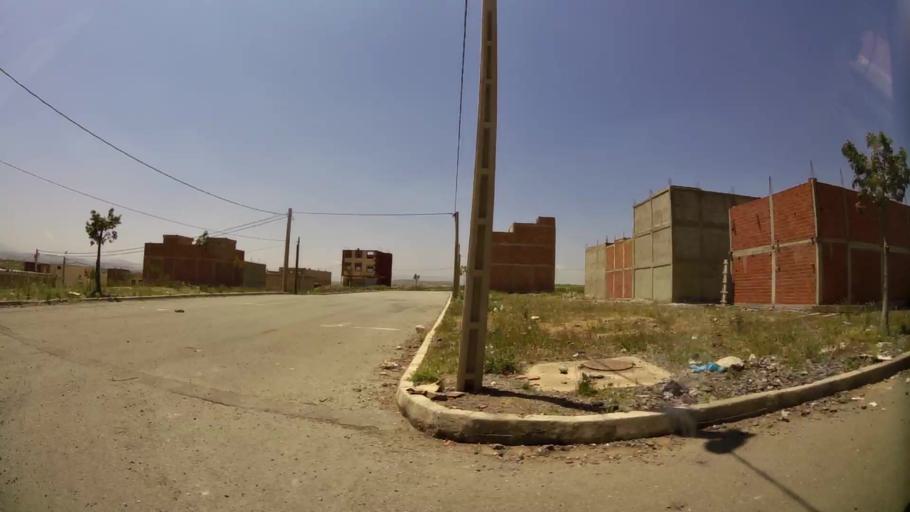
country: MA
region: Oriental
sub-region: Oujda-Angad
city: Oujda
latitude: 34.6756
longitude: -1.9527
